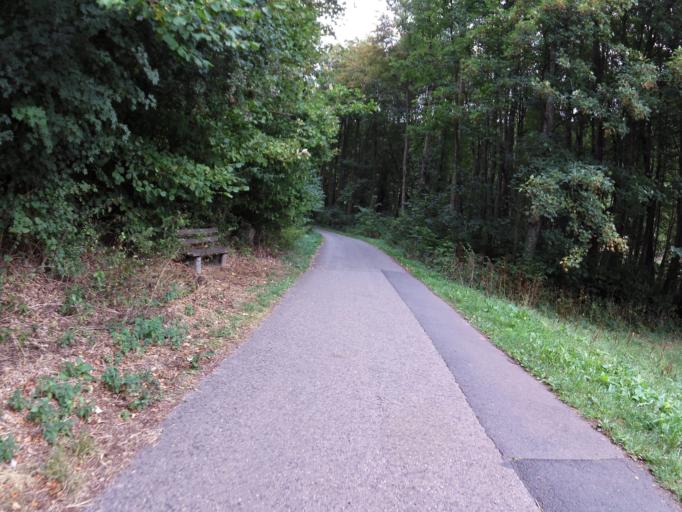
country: DE
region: North Rhine-Westphalia
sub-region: Regierungsbezirk Koln
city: Nettersheim
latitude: 50.5121
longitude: 6.5851
